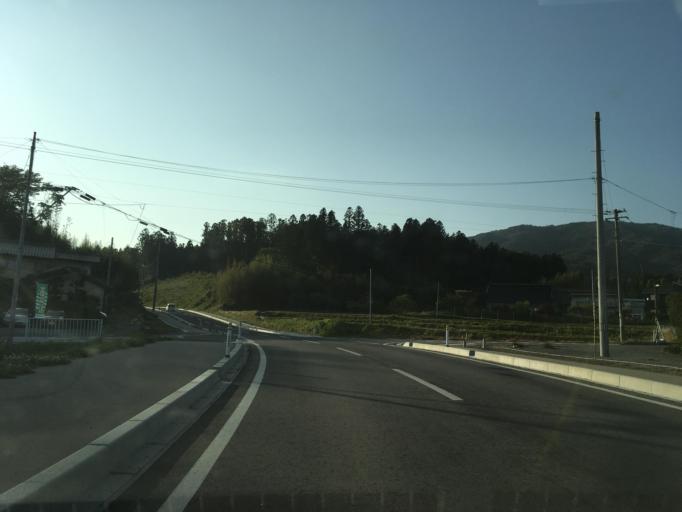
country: JP
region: Iwate
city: Ofunato
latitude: 39.0188
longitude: 141.6667
